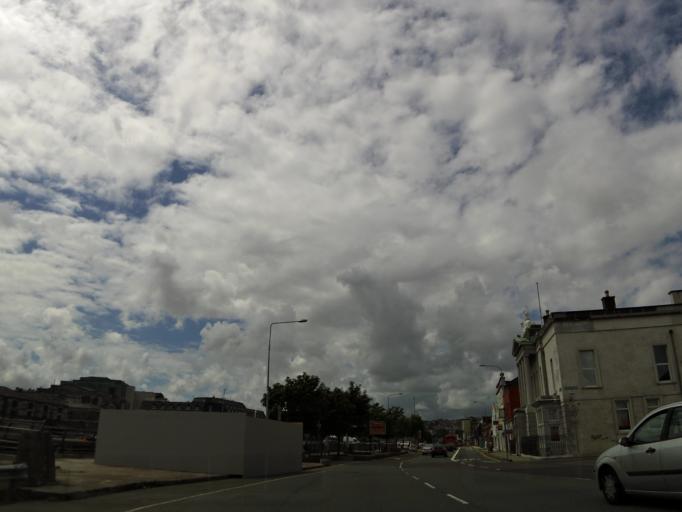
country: IE
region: Munster
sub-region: County Cork
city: Cork
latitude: 51.9000
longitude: -8.4610
